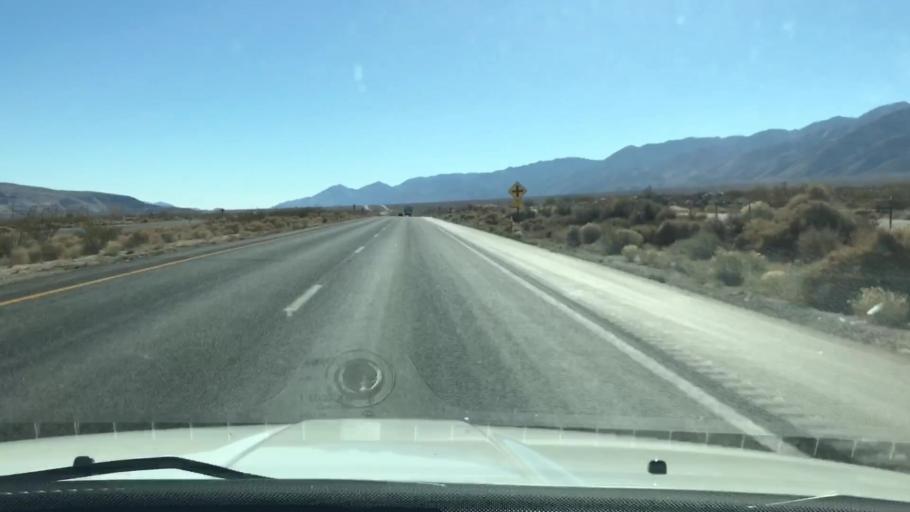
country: US
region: California
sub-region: Inyo County
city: Lone Pine
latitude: 36.1872
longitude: -117.9788
